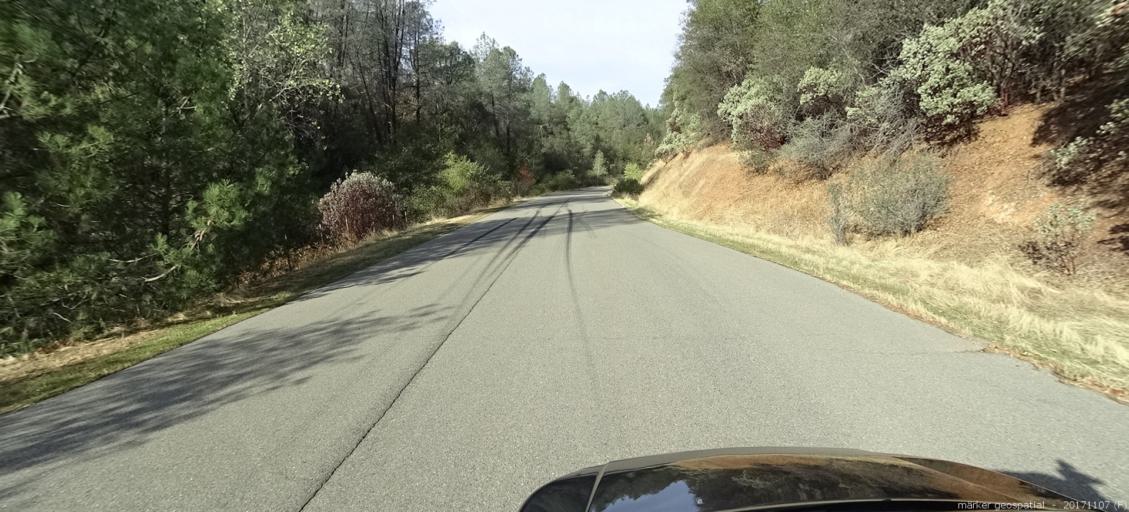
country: US
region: California
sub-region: Shasta County
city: Redding
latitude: 40.5683
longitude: -122.4420
